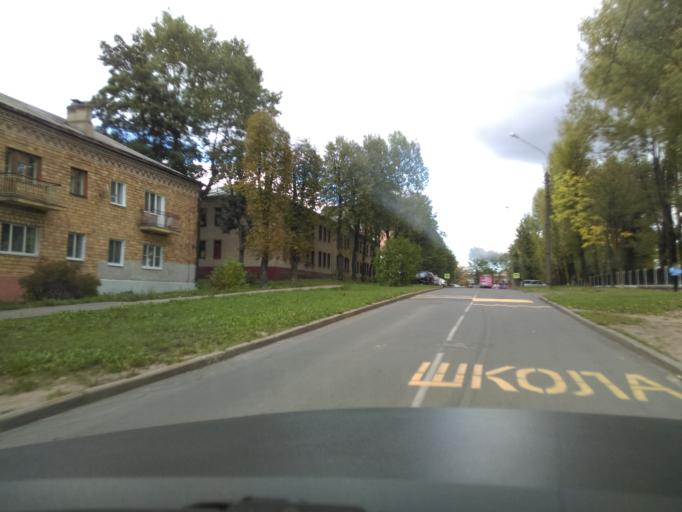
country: BY
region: Minsk
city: Minsk
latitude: 53.9090
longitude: 27.6289
